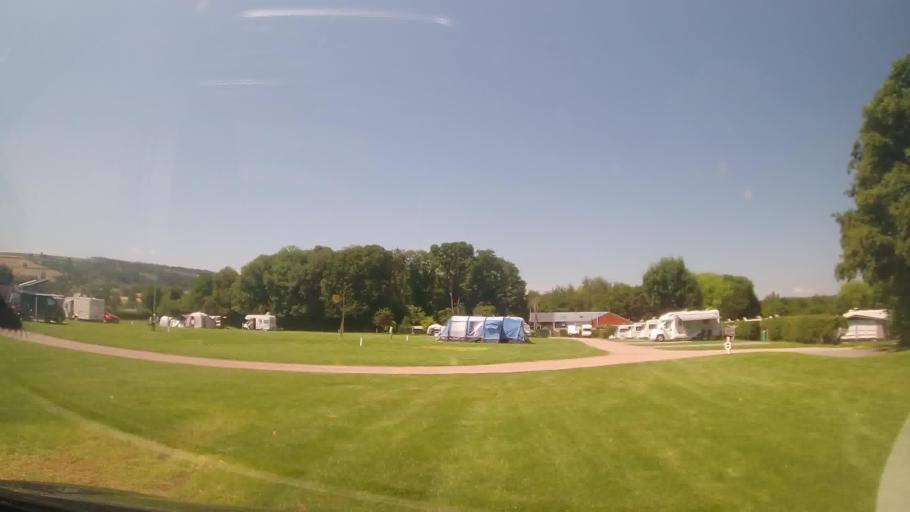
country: GB
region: England
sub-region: Herefordshire
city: Ocle Pychard
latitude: 52.0649
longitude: -2.5421
